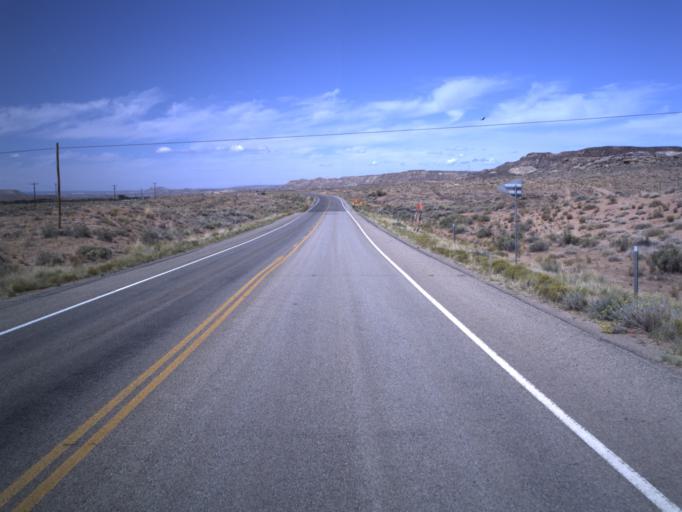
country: US
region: Colorado
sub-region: Montezuma County
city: Towaoc
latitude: 37.2108
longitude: -109.1726
